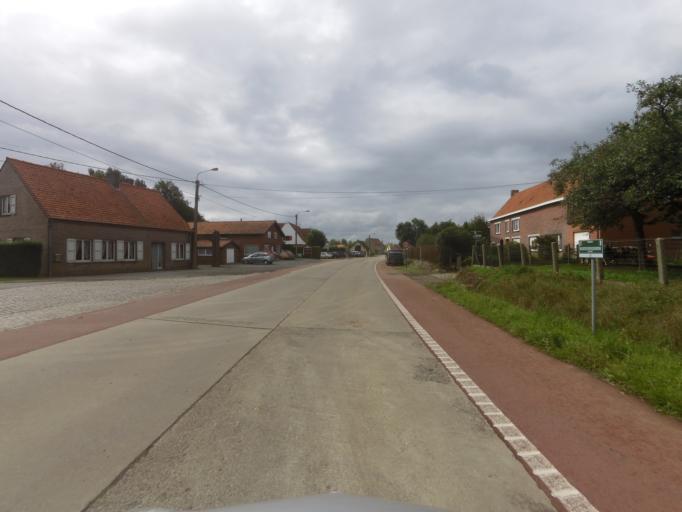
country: BE
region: Flanders
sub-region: Provincie West-Vlaanderen
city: Lichtervelde
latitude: 51.0618
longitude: 3.1377
